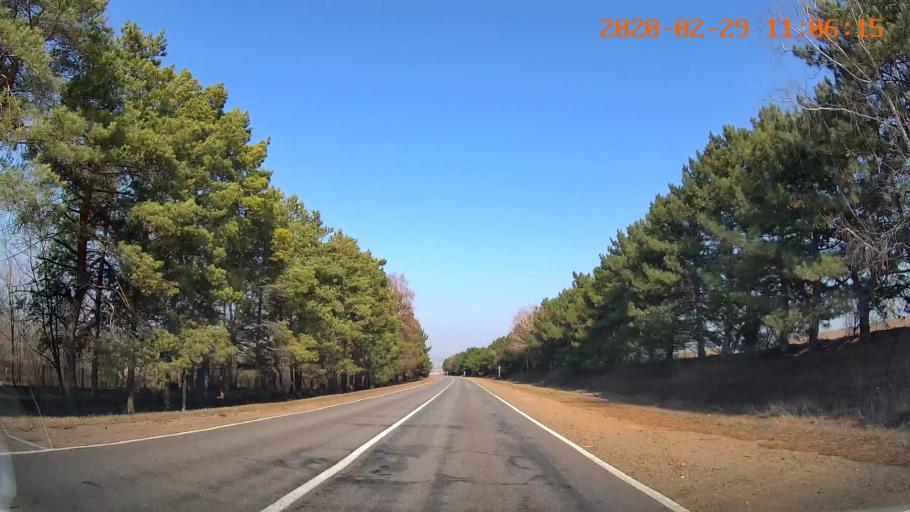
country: MD
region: Criuleni
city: Criuleni
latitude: 47.2124
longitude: 29.1889
